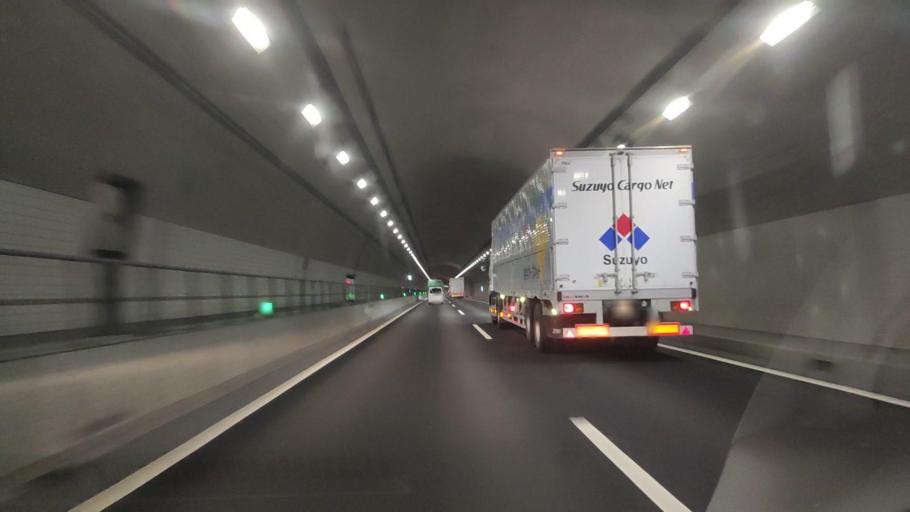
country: JP
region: Tokyo
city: Hachioji
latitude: 35.5705
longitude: 139.3041
